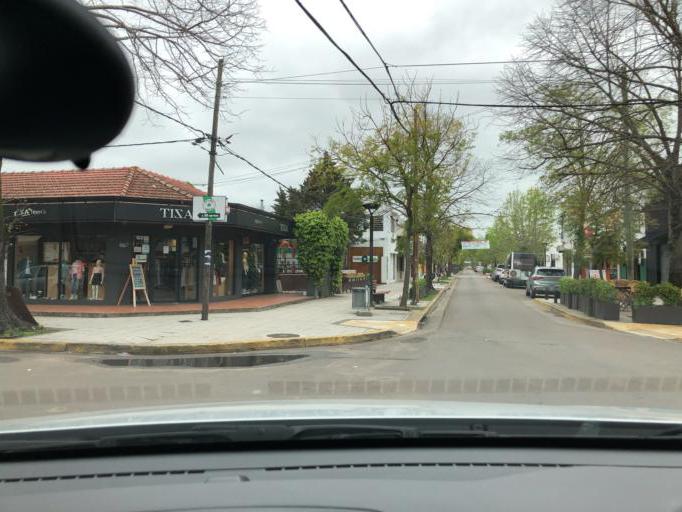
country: AR
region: Buenos Aires
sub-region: Partido de La Plata
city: La Plata
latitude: -34.8687
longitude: -58.0442
